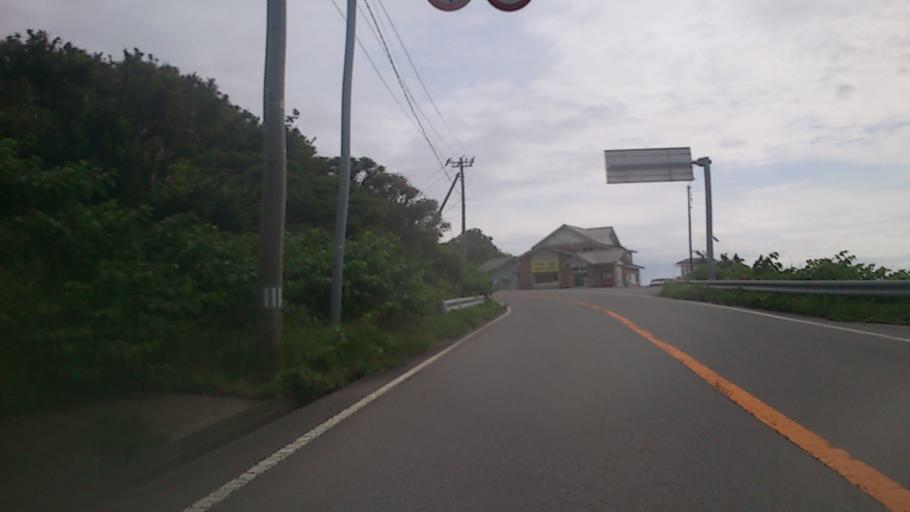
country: JP
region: Akita
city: Noshiromachi
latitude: 40.4334
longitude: 139.9413
